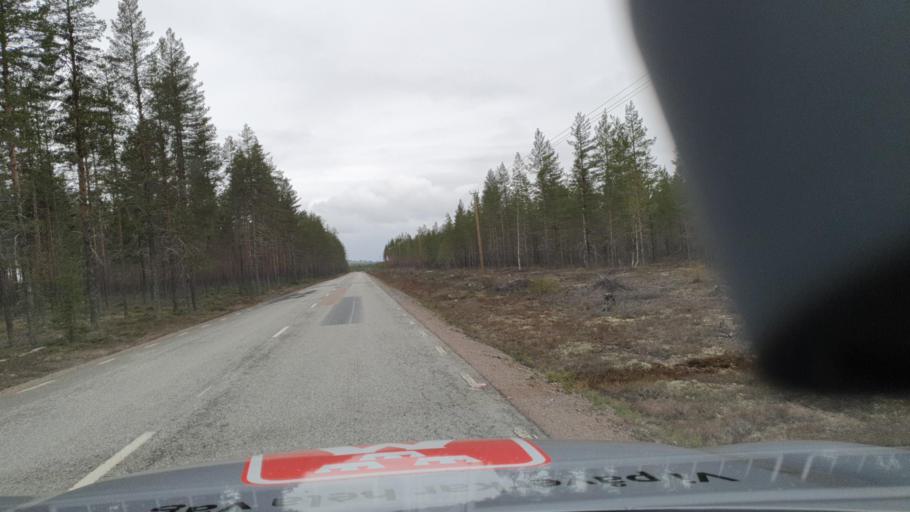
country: SE
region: Vaesternorrland
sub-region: Solleftea Kommun
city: Solleftea
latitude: 63.6170
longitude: 17.4865
